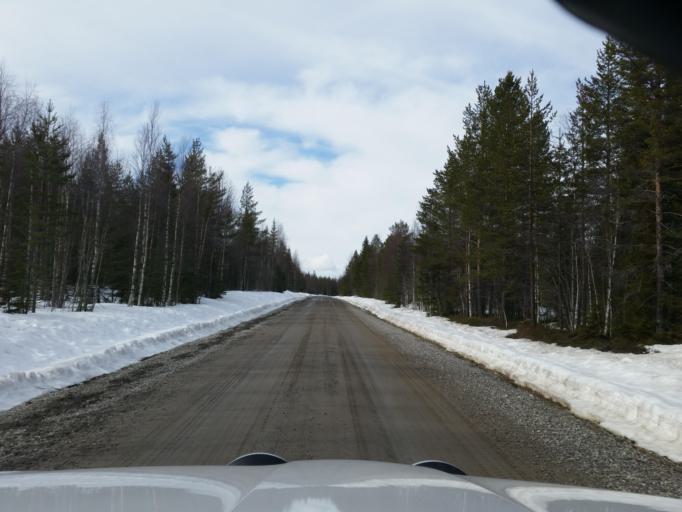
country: SE
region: Vaesterbotten
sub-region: Skelleftea Kommun
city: Storvik
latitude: 65.2155
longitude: 20.8683
